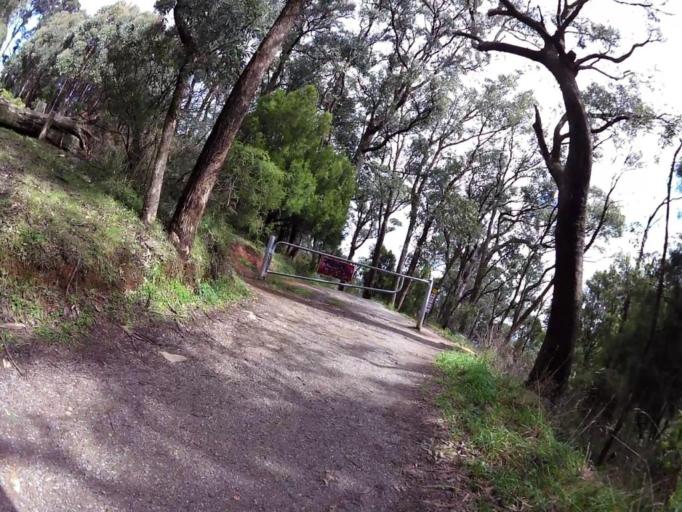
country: AU
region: Victoria
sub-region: Yarra Ranges
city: Montrose
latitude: -37.8333
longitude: 145.3488
